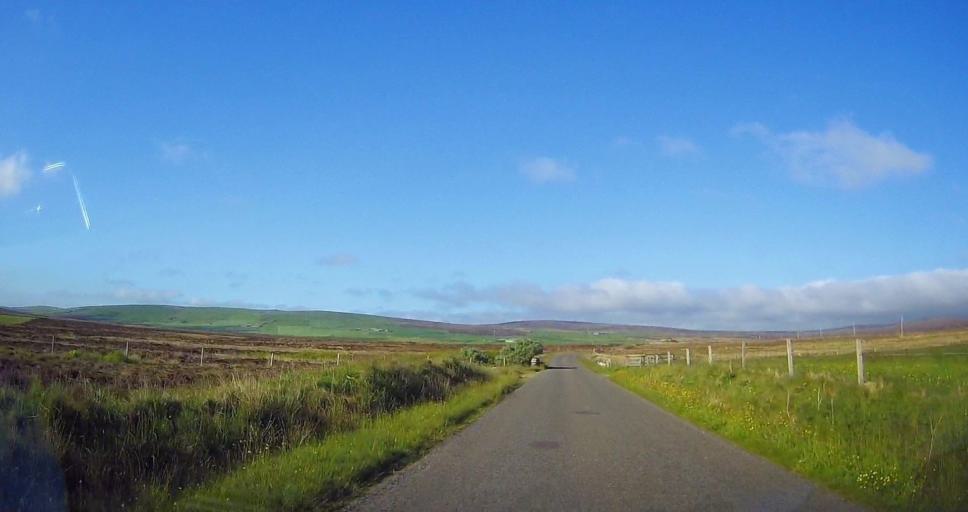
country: GB
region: Scotland
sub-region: Orkney Islands
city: Stromness
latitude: 59.0778
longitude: -3.2013
